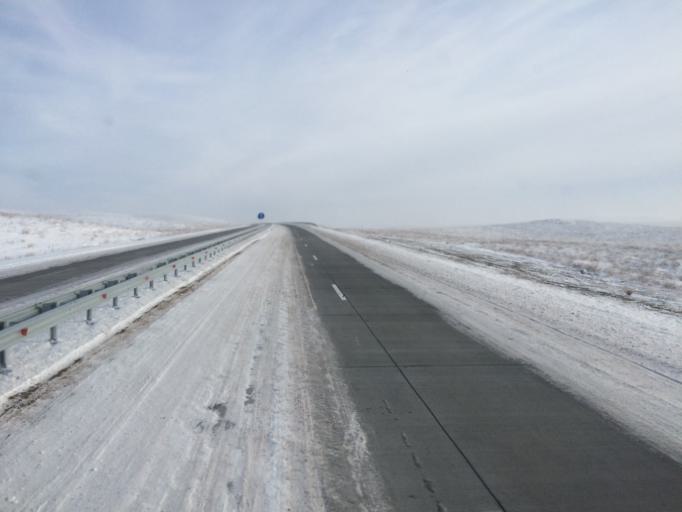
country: KZ
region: Zhambyl
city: Georgiyevka
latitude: 43.3400
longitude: 74.4582
